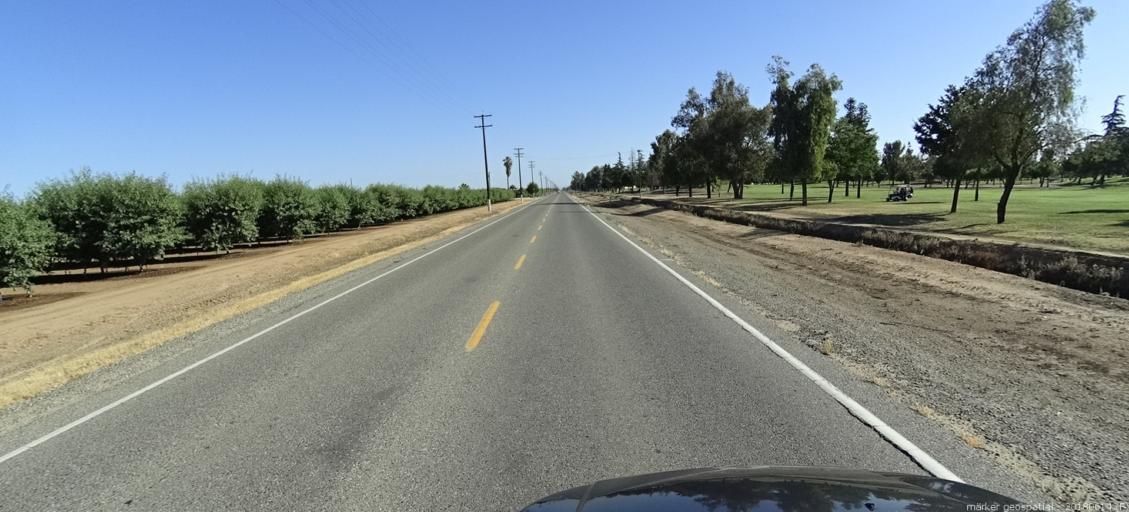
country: US
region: California
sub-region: Madera County
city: Madera Acres
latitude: 36.9874
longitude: -120.1286
